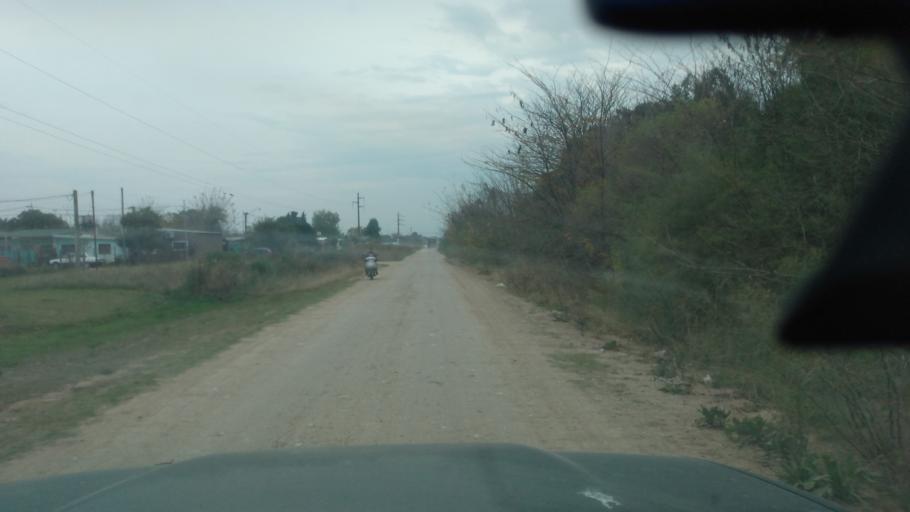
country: AR
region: Buenos Aires
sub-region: Partido de Lujan
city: Lujan
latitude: -34.5618
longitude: -59.1437
